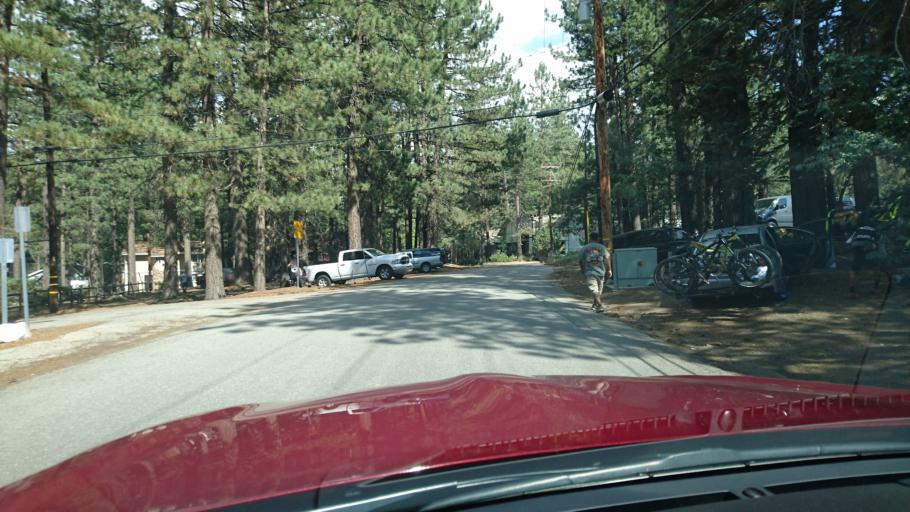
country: US
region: California
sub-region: San Bernardino County
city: Big Bear Lake
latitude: 34.2376
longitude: -116.8883
